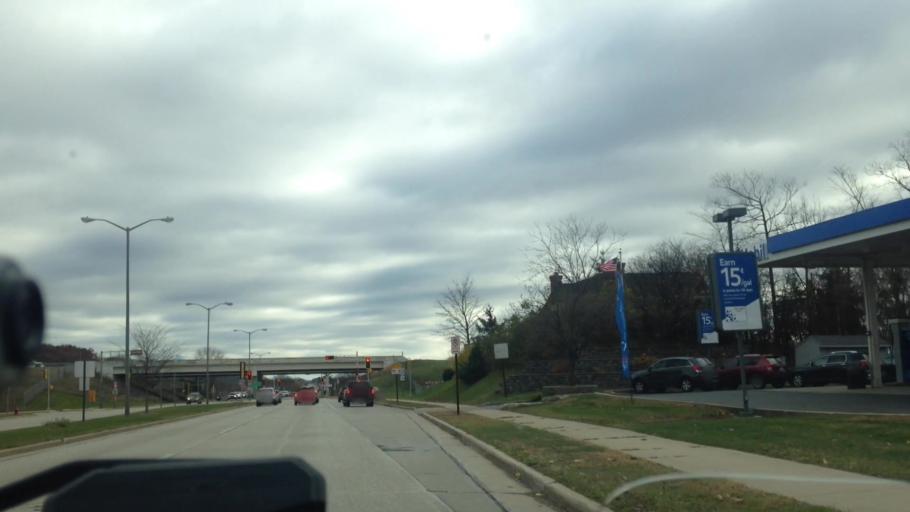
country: US
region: Wisconsin
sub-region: Washington County
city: West Bend
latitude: 43.4271
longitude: -88.2108
